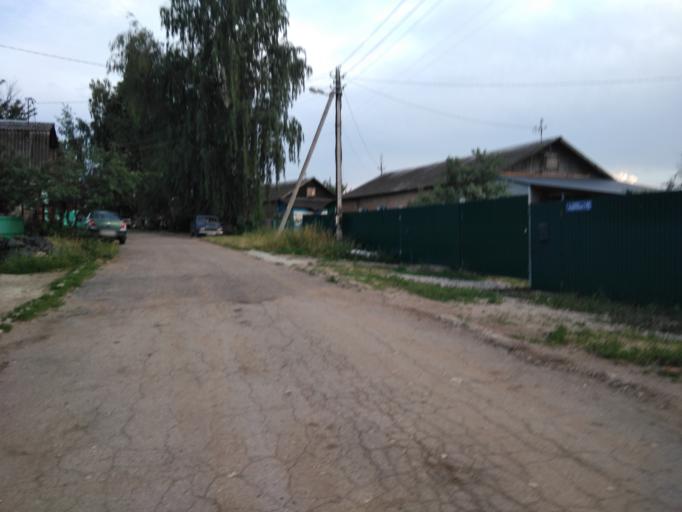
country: RU
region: Tula
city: Lomintsevskiy
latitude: 53.9359
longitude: 37.6205
